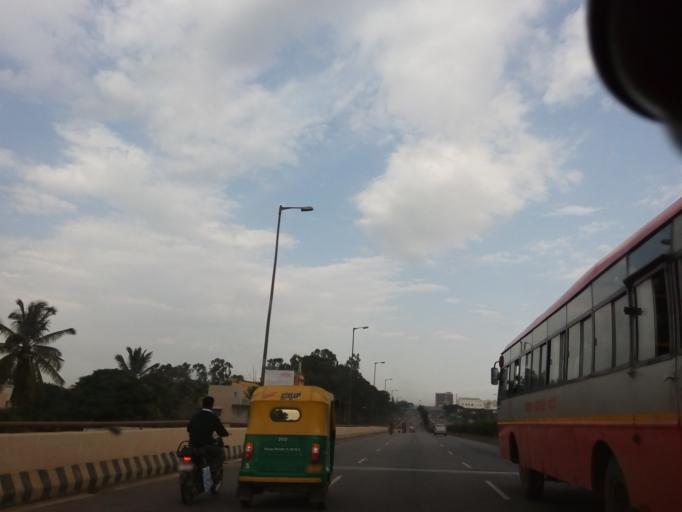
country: IN
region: Karnataka
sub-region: Bangalore Rural
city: Nelamangala
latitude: 13.0529
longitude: 77.4857
